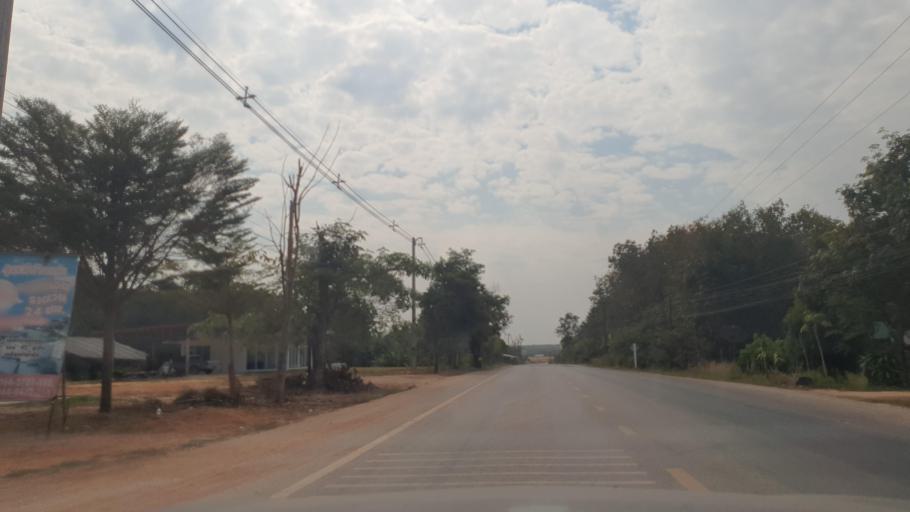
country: TH
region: Changwat Bueng Kan
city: Si Wilai
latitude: 18.2963
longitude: 103.8013
